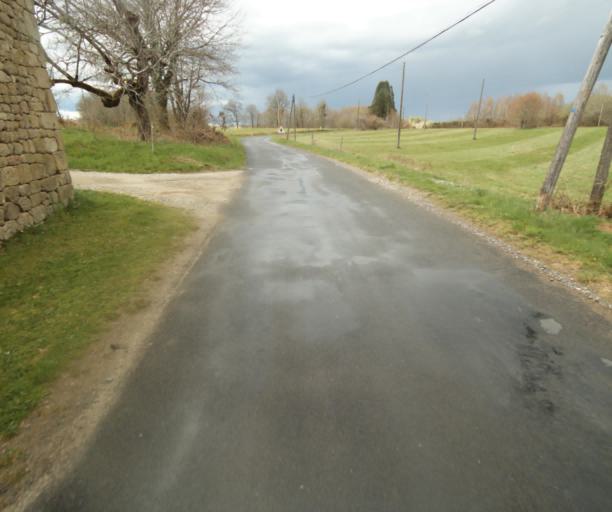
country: FR
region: Limousin
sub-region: Departement de la Correze
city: Egletons
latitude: 45.2595
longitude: 1.9911
